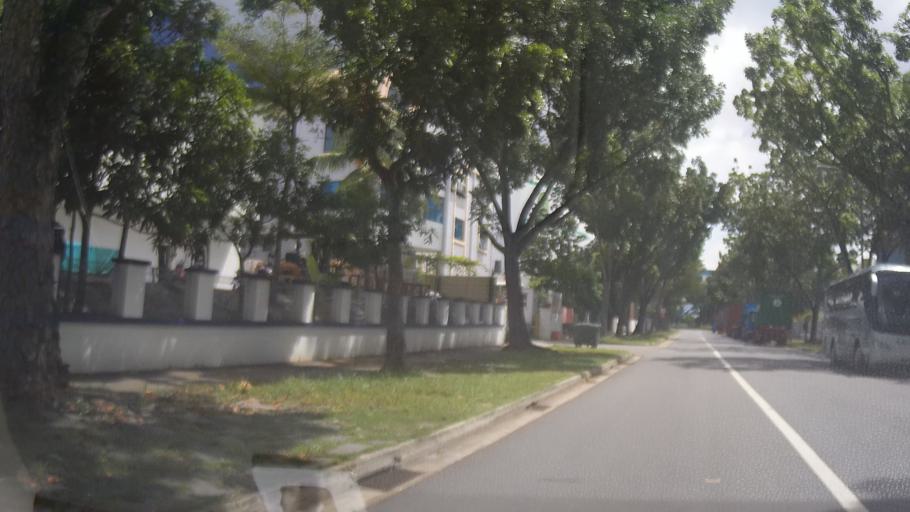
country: MY
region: Johor
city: Johor Bahru
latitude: 1.4099
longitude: 103.7450
